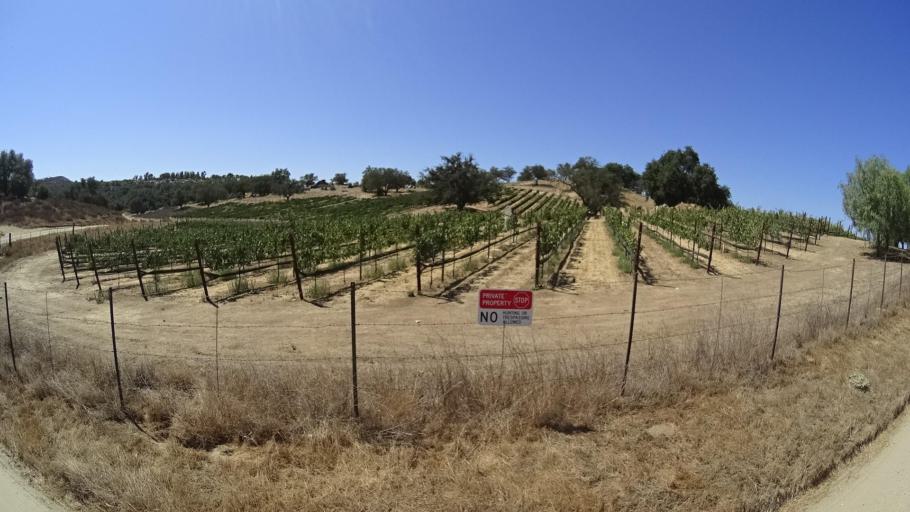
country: US
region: California
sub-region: San Diego County
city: San Diego Country Estates
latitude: 33.0583
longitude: -116.7509
